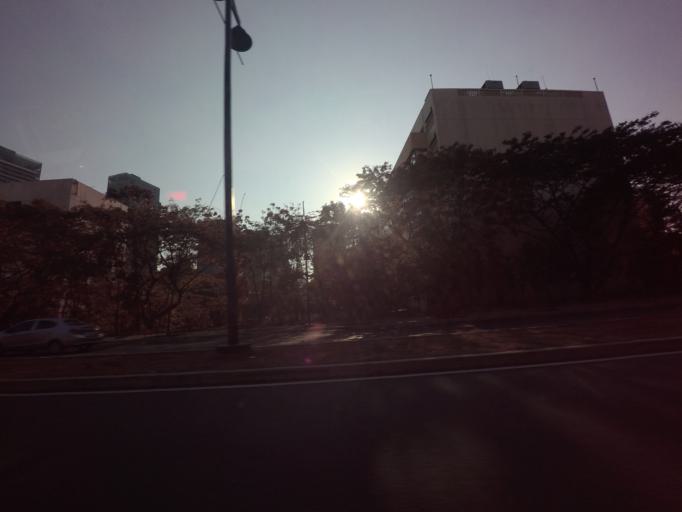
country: PH
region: Calabarzon
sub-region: Province of Rizal
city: Pateros
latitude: 14.5539
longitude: 121.0571
